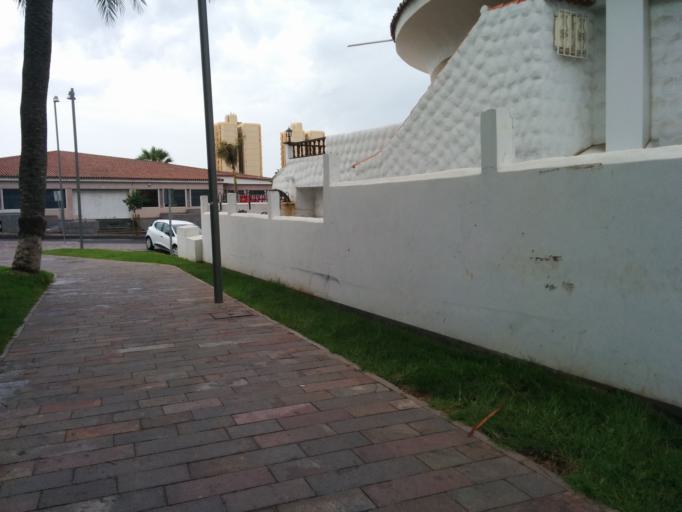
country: ES
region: Canary Islands
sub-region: Provincia de Santa Cruz de Tenerife
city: Playa de las Americas
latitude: 28.0683
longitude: -16.7278
